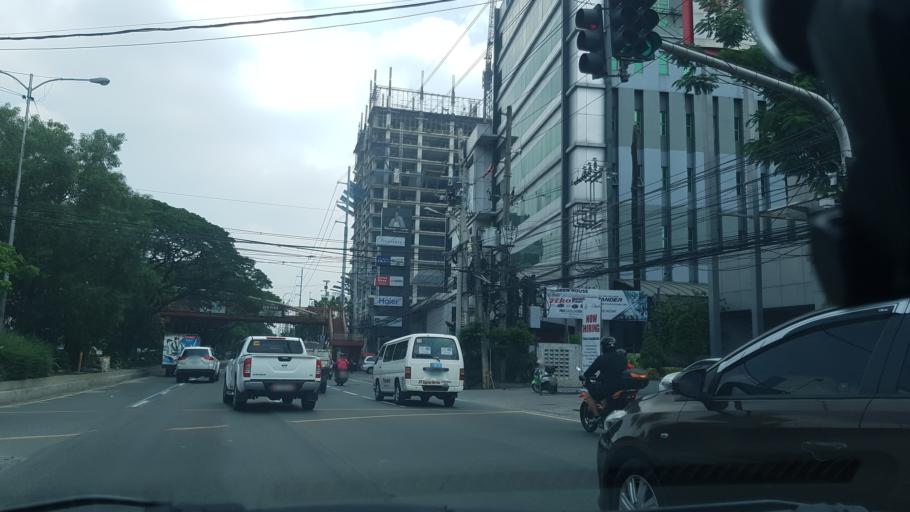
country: PH
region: Metro Manila
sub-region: Pasig
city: Pasig City
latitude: 14.5774
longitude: 121.0734
